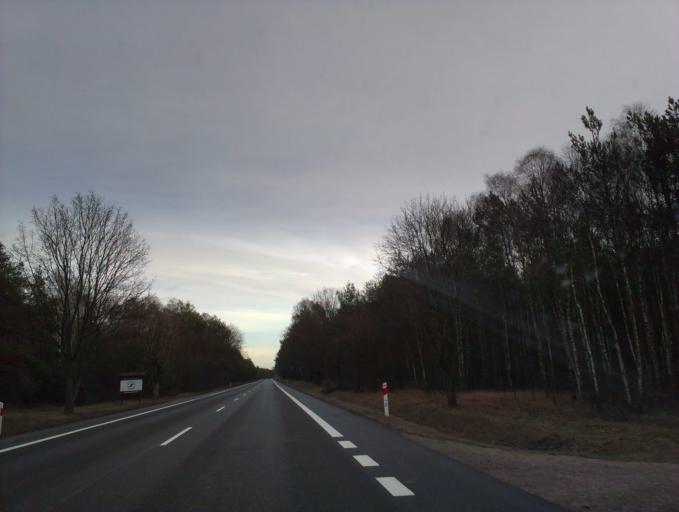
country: PL
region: Masovian Voivodeship
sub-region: Powiat sierpecki
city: Szczutowo
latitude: 52.8958
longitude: 19.5461
